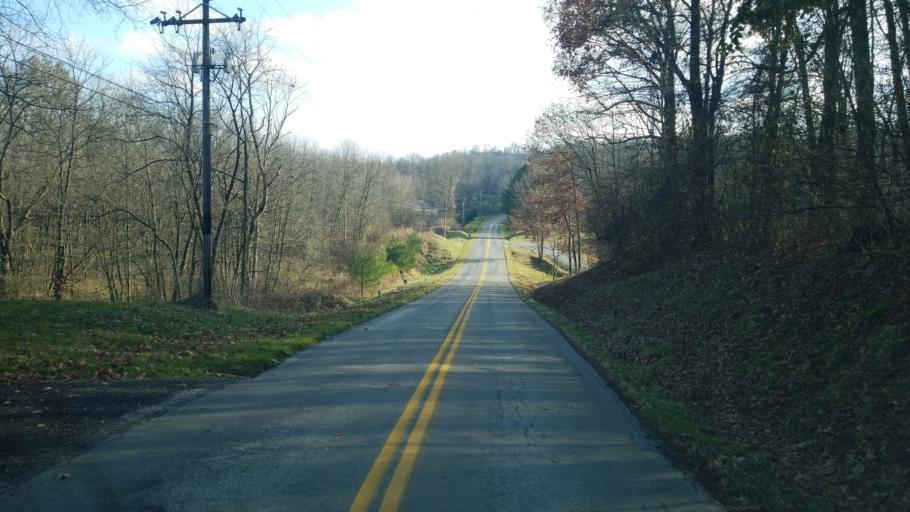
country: US
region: Ohio
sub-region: Ashland County
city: Loudonville
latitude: 40.6689
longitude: -82.3285
